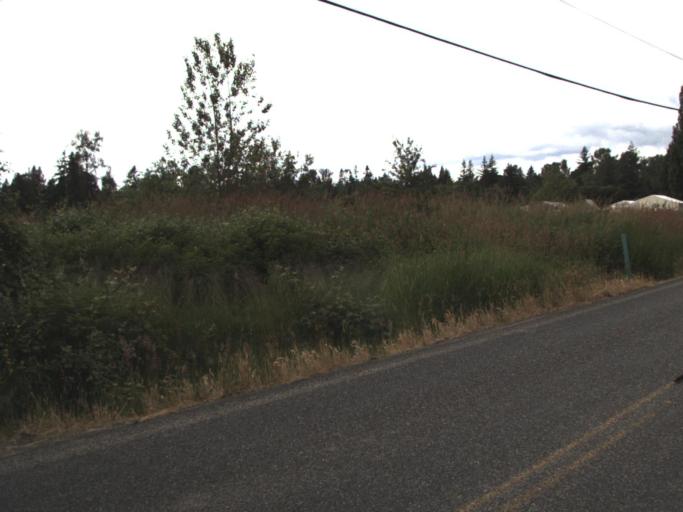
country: US
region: Washington
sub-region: Whatcom County
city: Birch Bay
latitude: 48.9381
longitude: -122.7262
